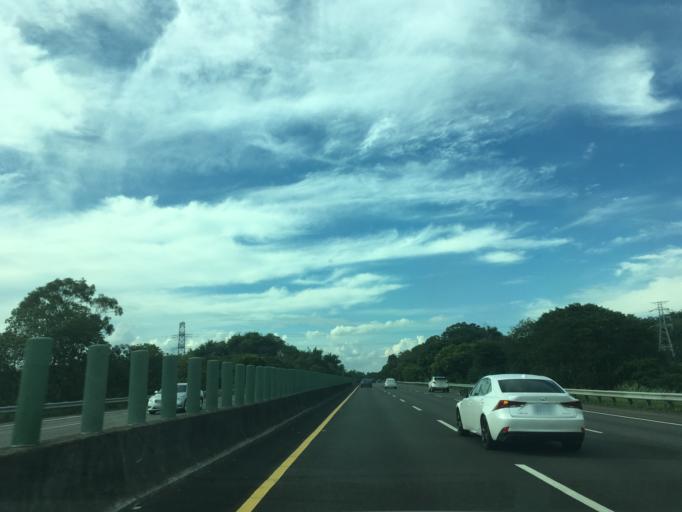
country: TW
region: Taiwan
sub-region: Chiayi
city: Jiayi Shi
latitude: 23.5585
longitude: 120.5050
